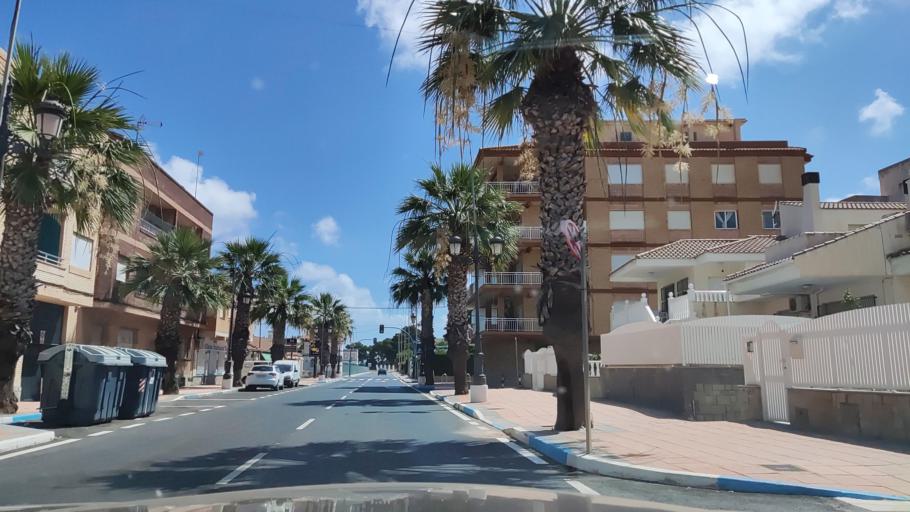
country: ES
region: Murcia
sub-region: Murcia
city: Los Alcazares
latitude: 37.7368
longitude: -0.8538
